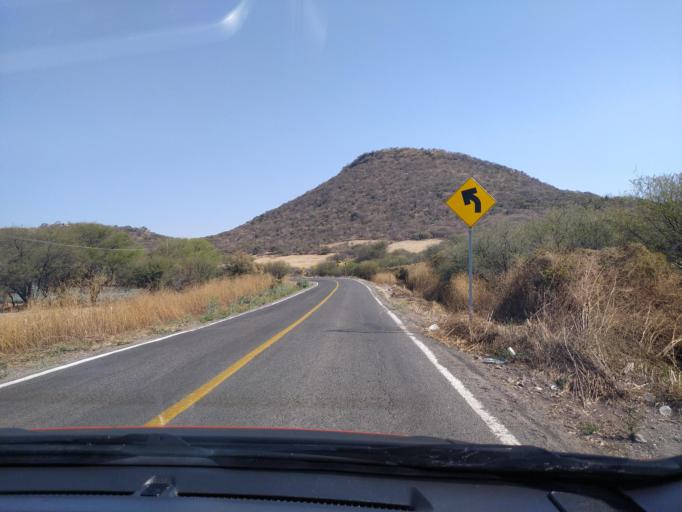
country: MX
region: Guanajuato
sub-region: San Francisco del Rincon
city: San Ignacio de Hidalgo
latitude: 20.7939
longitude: -101.8358
